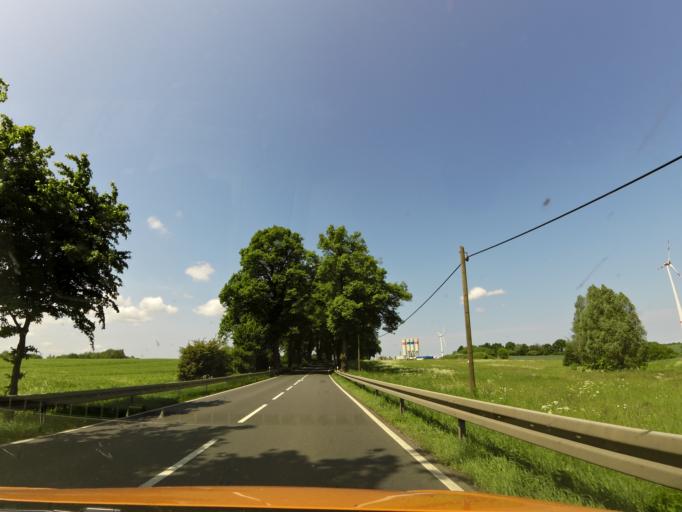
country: DE
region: Mecklenburg-Vorpommern
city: Carlow
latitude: 53.8292
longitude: 10.9598
